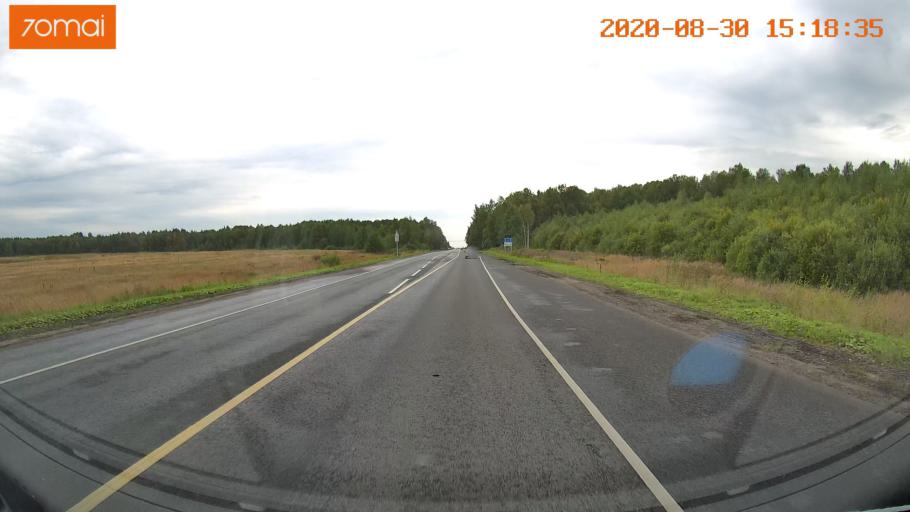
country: RU
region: Ivanovo
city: Rodniki
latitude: 57.1214
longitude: 41.7920
